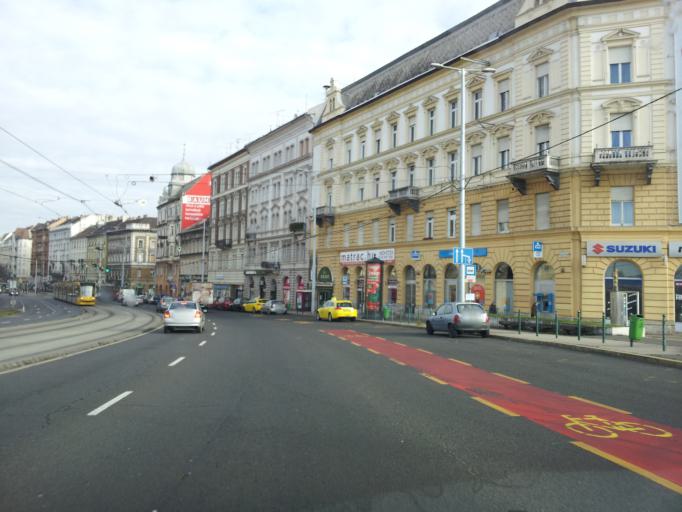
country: HU
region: Budapest
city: Budapest IX. keruelet
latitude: 47.4806
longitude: 19.0673
